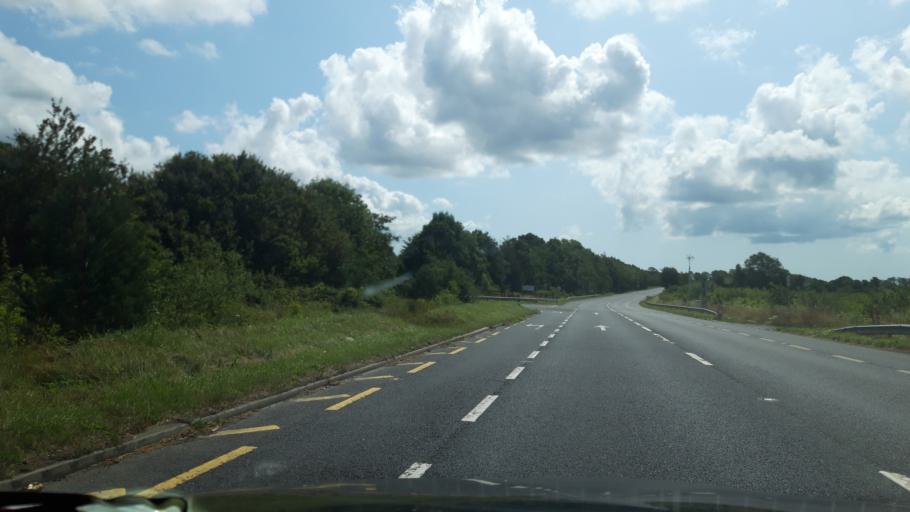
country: IE
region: Munster
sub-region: Waterford
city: Waterford
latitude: 52.2806
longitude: -7.0602
